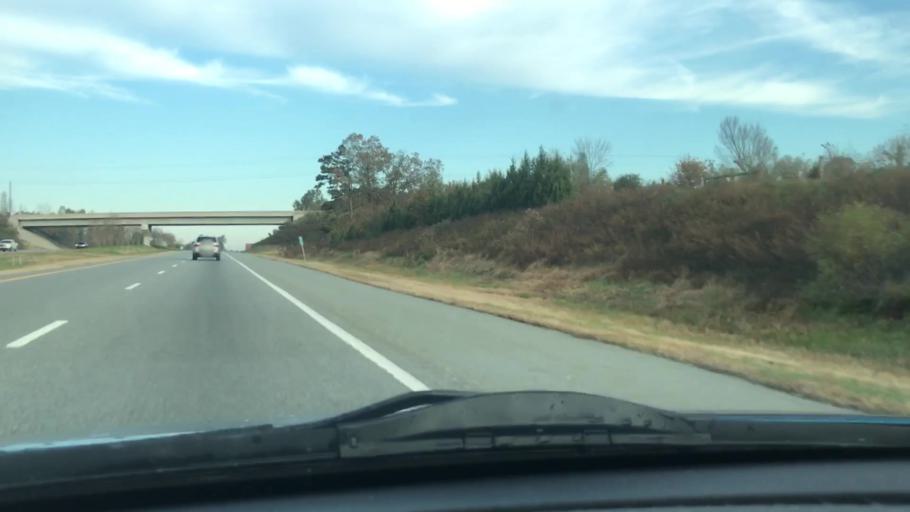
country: US
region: North Carolina
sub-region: Randolph County
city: Archdale
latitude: 35.9183
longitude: -79.9166
